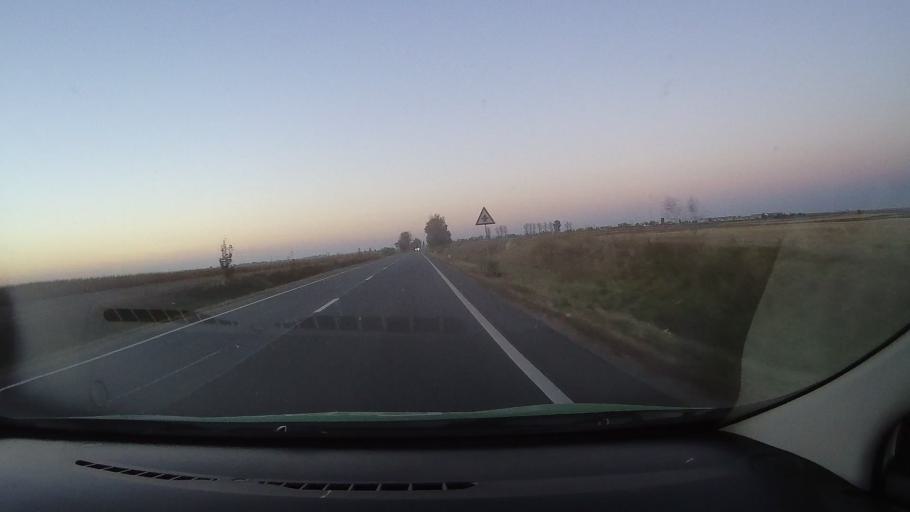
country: RO
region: Bihor
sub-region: Comuna Tarcea
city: Tarcea
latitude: 47.4741
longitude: 22.1644
